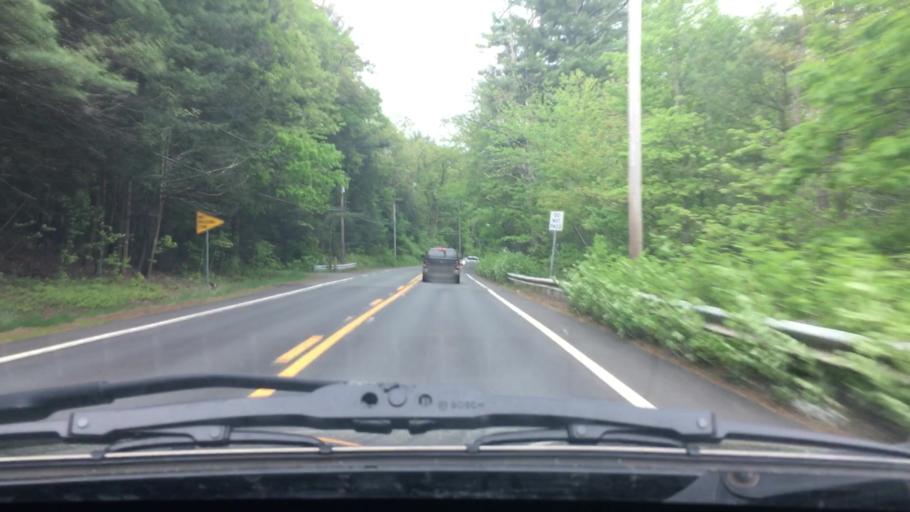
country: US
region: Massachusetts
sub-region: Franklin County
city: Leverett
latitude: 42.4586
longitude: -72.5207
